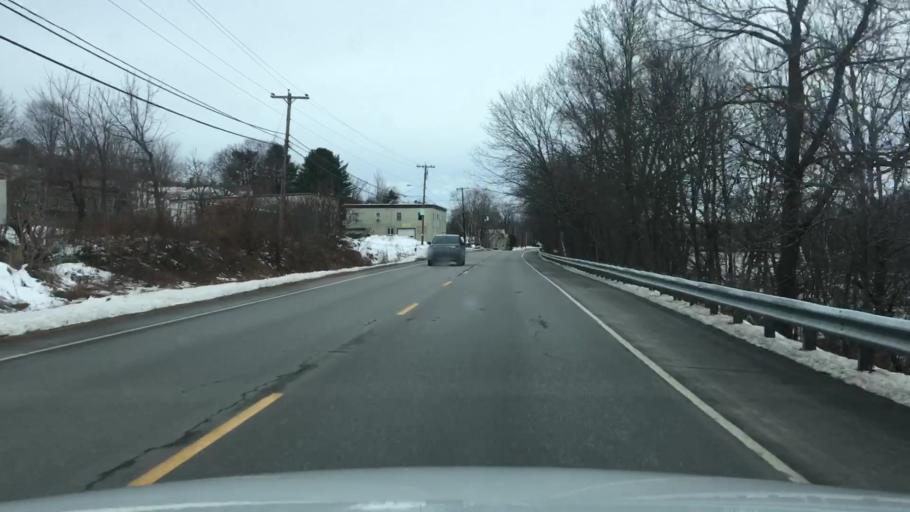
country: US
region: Maine
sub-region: Androscoggin County
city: Lewiston
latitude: 44.0694
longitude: -70.2090
